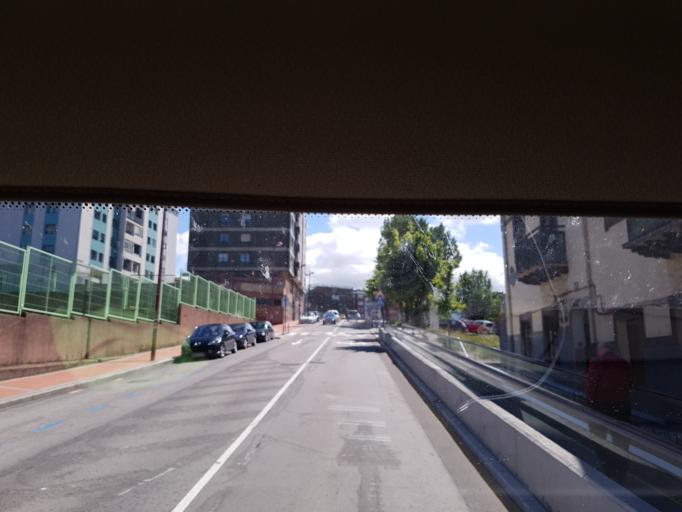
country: ES
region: Basque Country
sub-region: Bizkaia
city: Barakaldo
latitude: 43.2870
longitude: -2.9820
